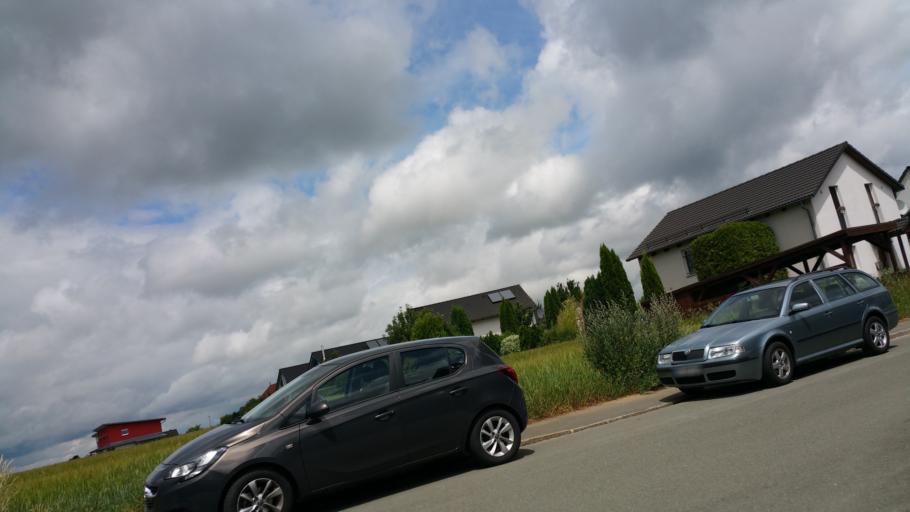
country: DE
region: Bavaria
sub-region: Upper Franconia
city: Rehau
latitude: 50.2395
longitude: 12.0151
